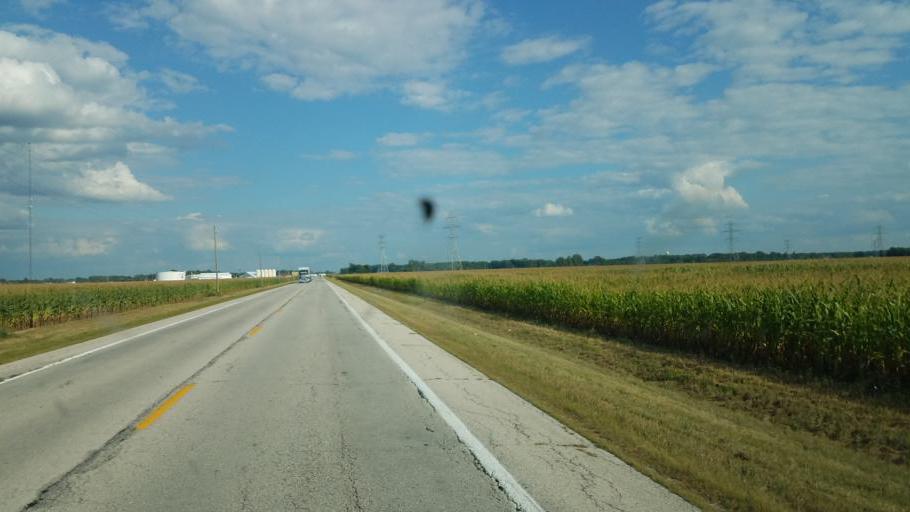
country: US
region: Ohio
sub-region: Wood County
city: Pemberville
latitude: 41.3478
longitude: -83.4521
